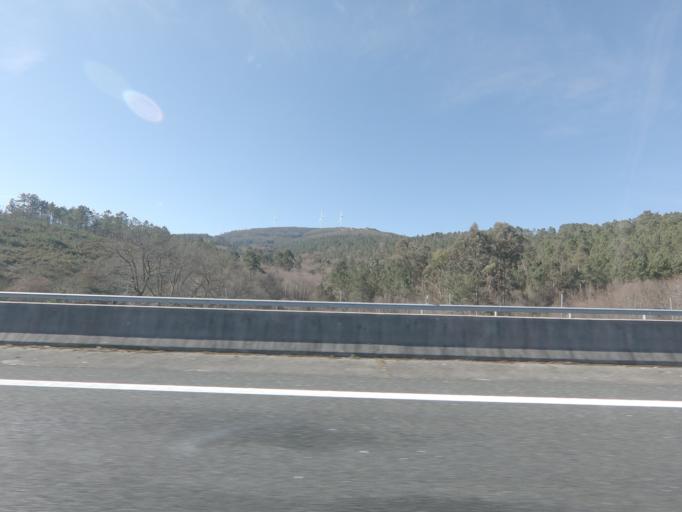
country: ES
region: Galicia
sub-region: Provincia de Ourense
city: Pinor
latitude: 42.5088
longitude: -8.0224
